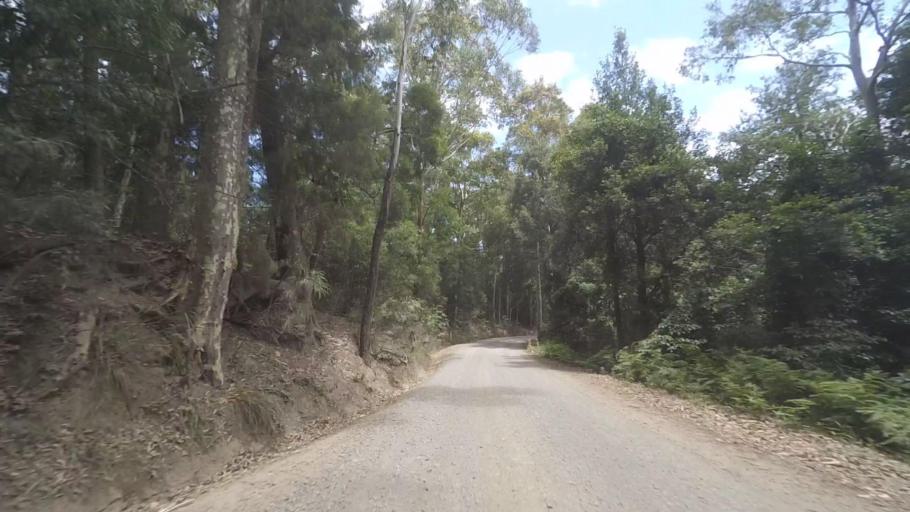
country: AU
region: New South Wales
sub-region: Shoalhaven Shire
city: Milton
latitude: -35.4349
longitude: 150.3320
